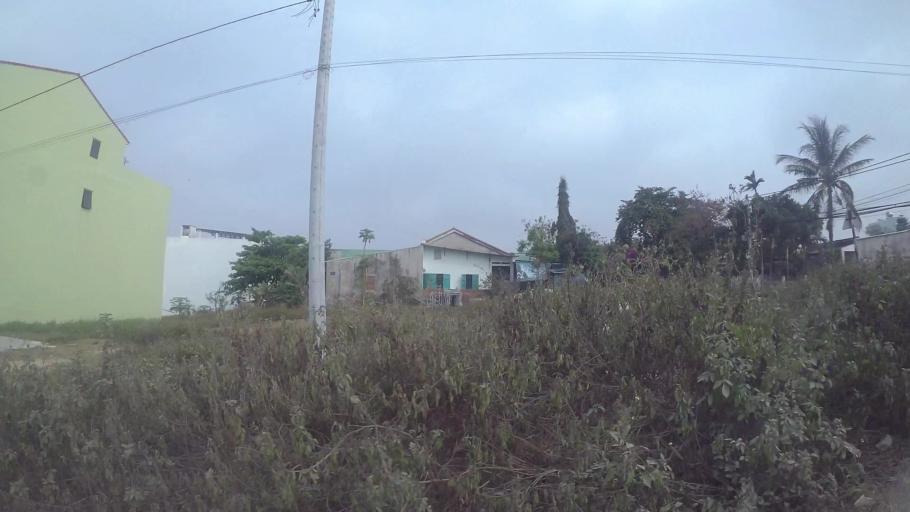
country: VN
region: Da Nang
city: Ngu Hanh Son
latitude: 16.0243
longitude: 108.2454
